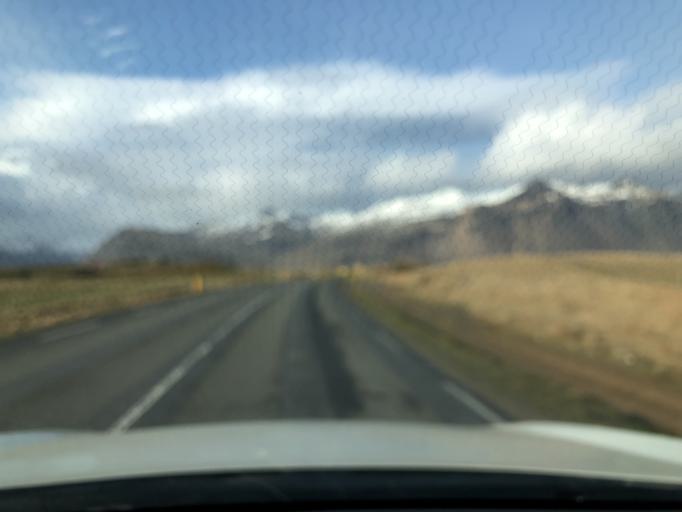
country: IS
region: East
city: Hoefn
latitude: 64.2809
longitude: -15.1923
